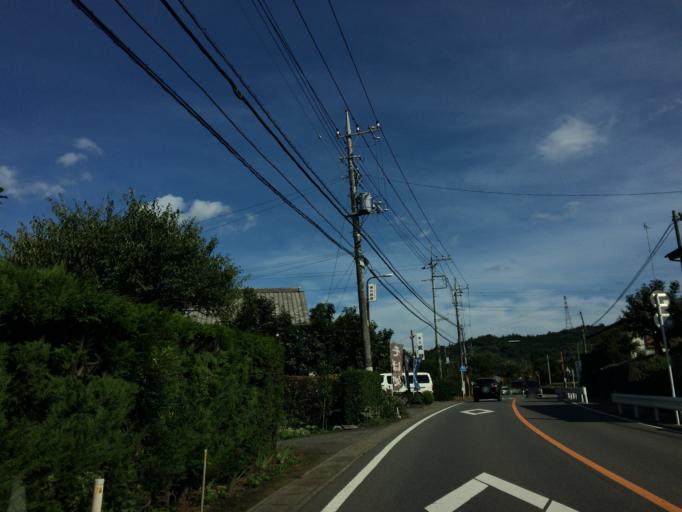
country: JP
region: Gunma
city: Nakanojomachi
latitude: 36.5752
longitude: 138.8498
